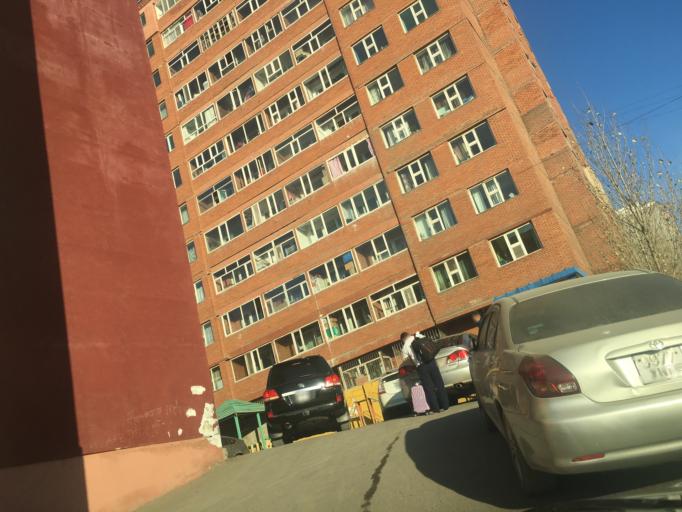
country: MN
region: Ulaanbaatar
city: Ulaanbaatar
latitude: 47.9175
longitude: 106.8813
